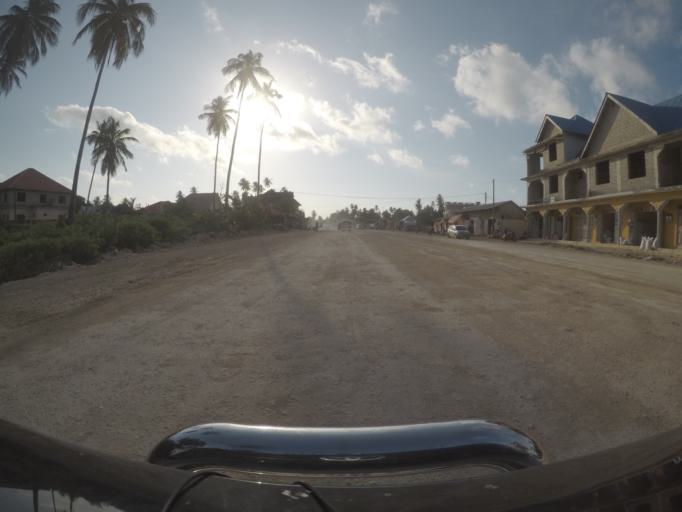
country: TZ
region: Zanzibar Central/South
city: Koani
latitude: -6.1954
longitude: 39.2691
